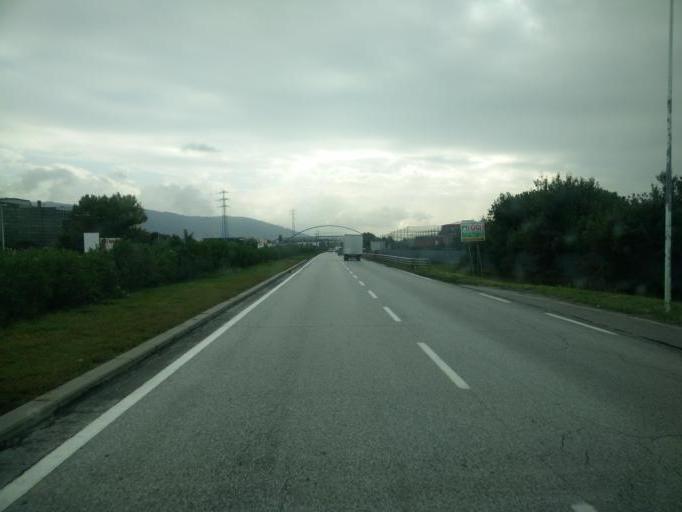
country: IT
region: Tuscany
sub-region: Provincia di Prato
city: Prato
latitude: 43.8777
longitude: 11.0692
